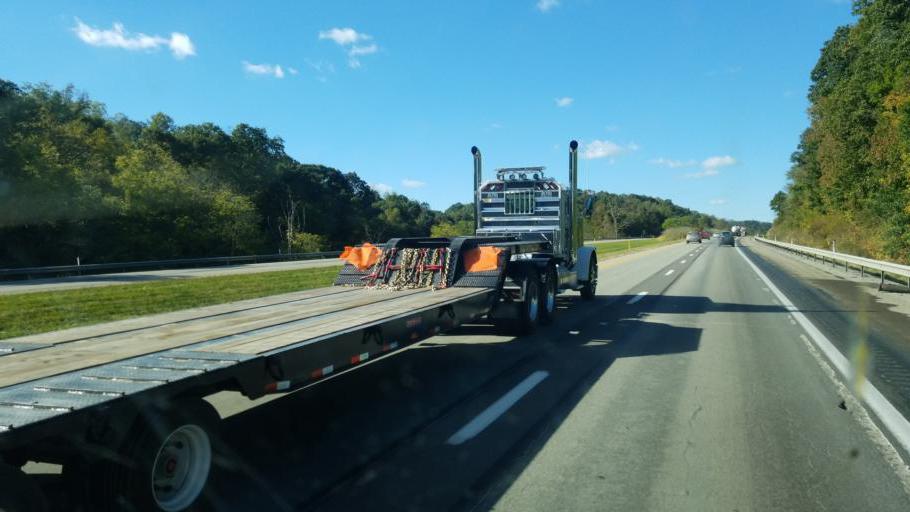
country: US
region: Pennsylvania
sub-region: Washington County
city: East Washington
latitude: 40.0442
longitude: -80.1818
